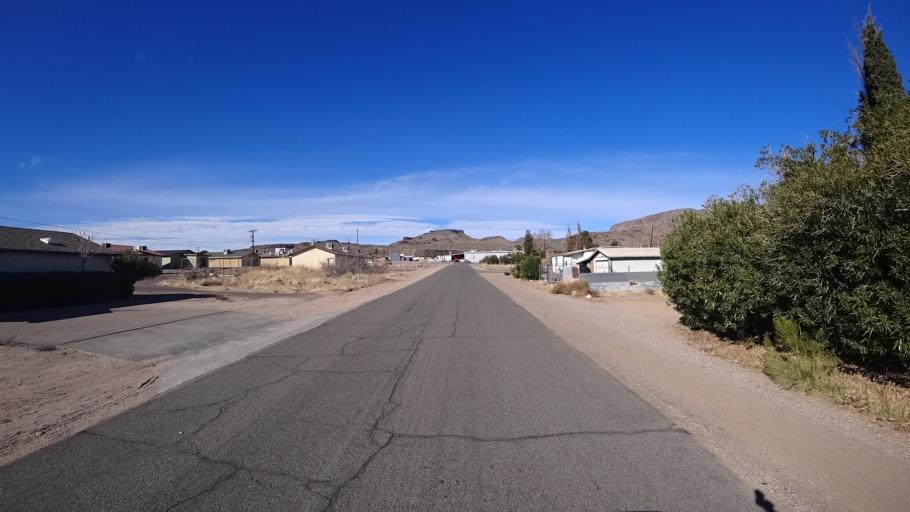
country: US
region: Arizona
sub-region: Mohave County
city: New Kingman-Butler
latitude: 35.2548
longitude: -114.0346
